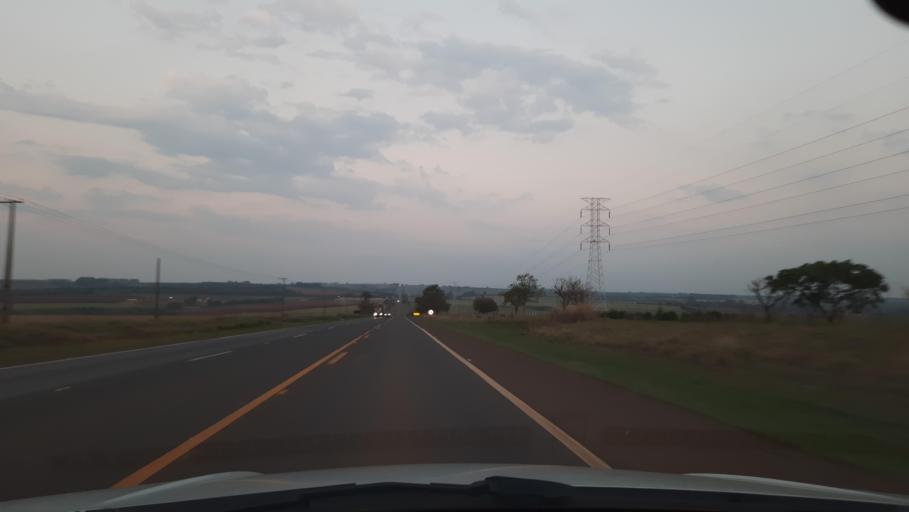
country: BR
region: Sao Paulo
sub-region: Casa Branca
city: Casa Branca
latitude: -21.8053
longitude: -47.1612
